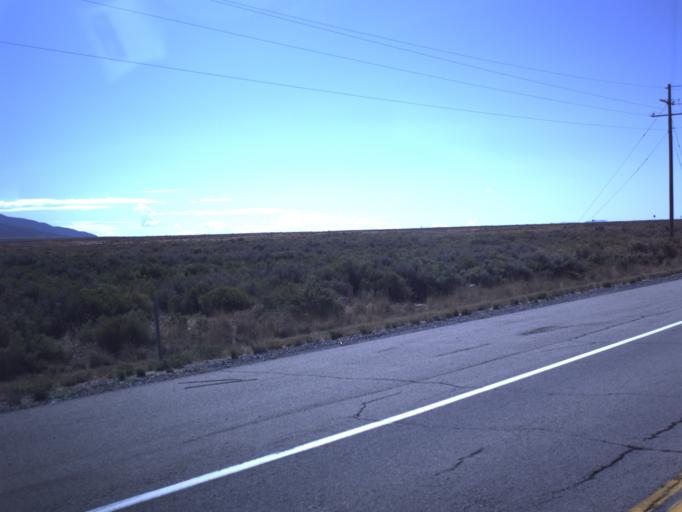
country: US
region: Utah
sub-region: Tooele County
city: Tooele
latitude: 40.3850
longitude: -112.3864
